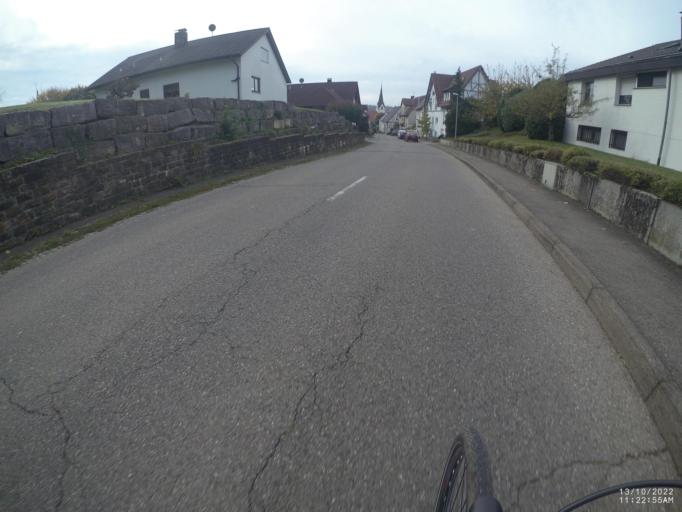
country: DE
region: Baden-Wuerttemberg
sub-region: Regierungsbezirk Stuttgart
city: Schlierbach
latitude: 48.6763
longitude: 9.5193
